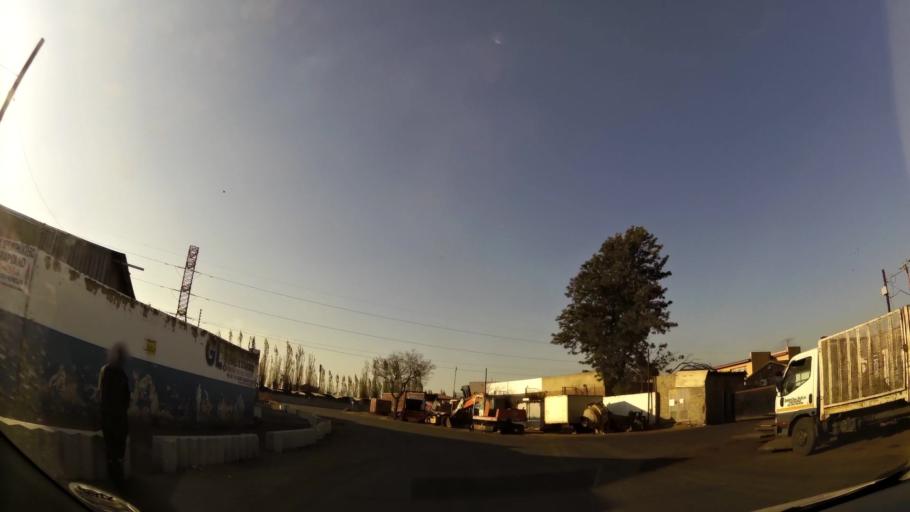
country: ZA
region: Gauteng
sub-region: West Rand District Municipality
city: Randfontein
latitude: -26.1930
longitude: 27.6867
